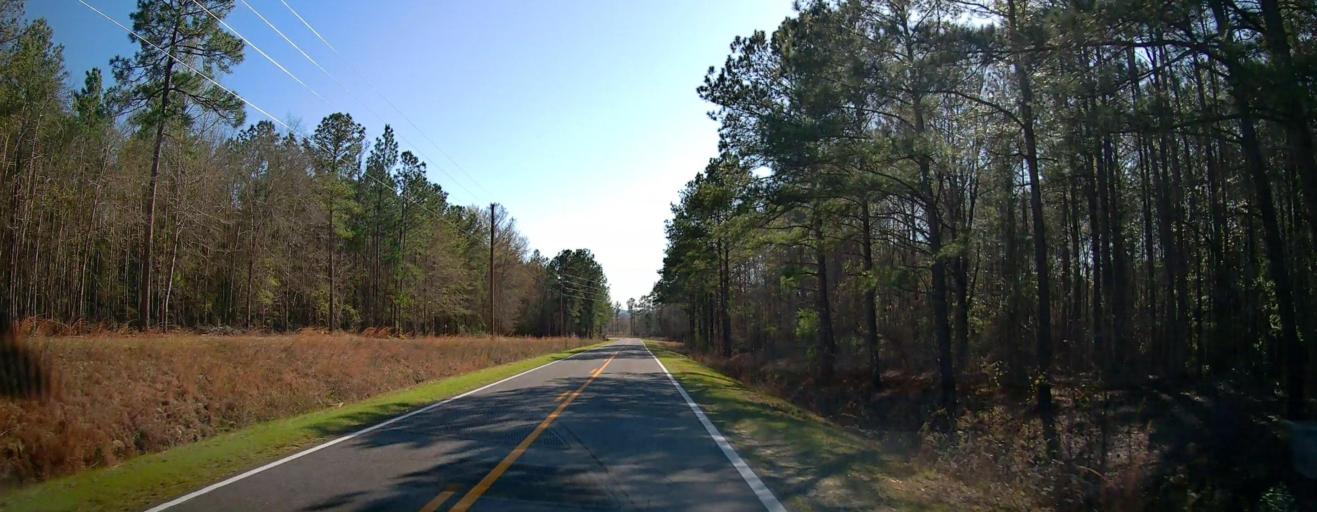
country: US
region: Georgia
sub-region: Taylor County
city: Reynolds
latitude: 32.5769
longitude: -83.9950
